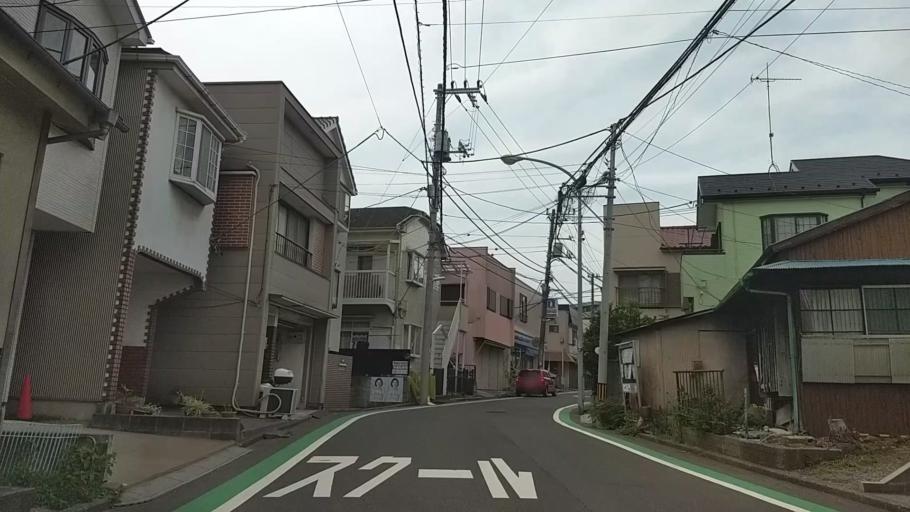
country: JP
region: Kanagawa
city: Yokohama
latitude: 35.4406
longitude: 139.6052
